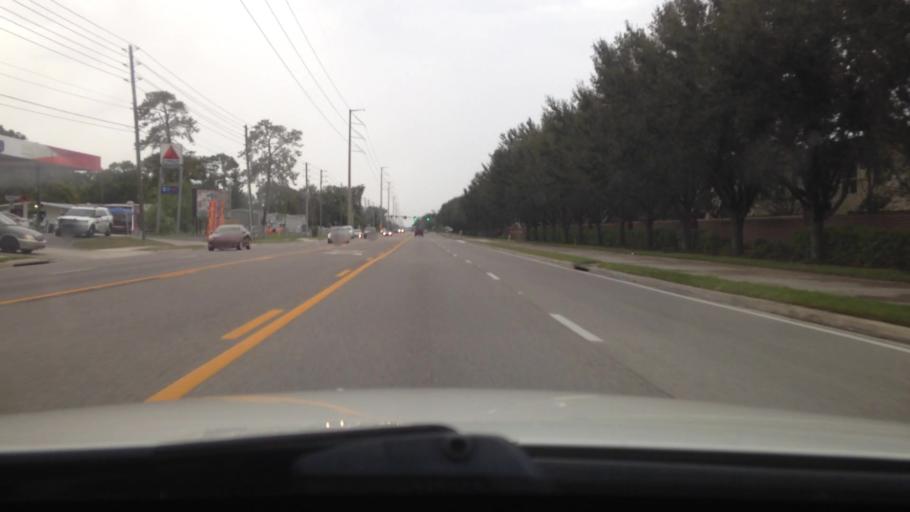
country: US
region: Florida
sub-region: Orange County
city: Apopka
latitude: 28.7102
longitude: -81.5091
